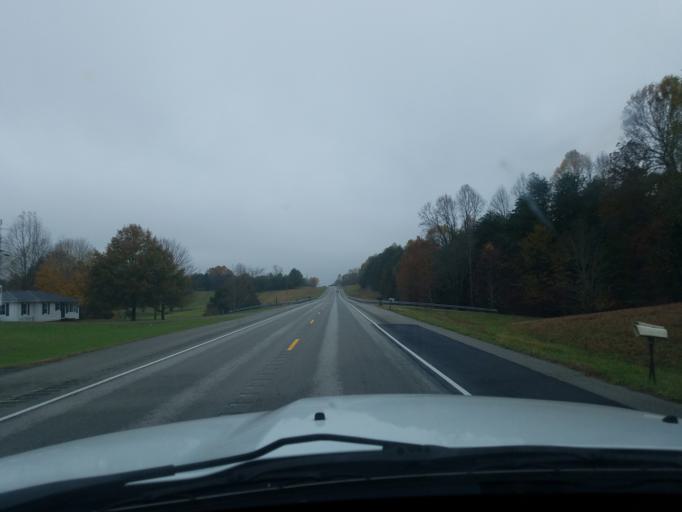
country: US
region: Kentucky
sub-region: Green County
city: Greensburg
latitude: 37.4040
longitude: -85.4790
